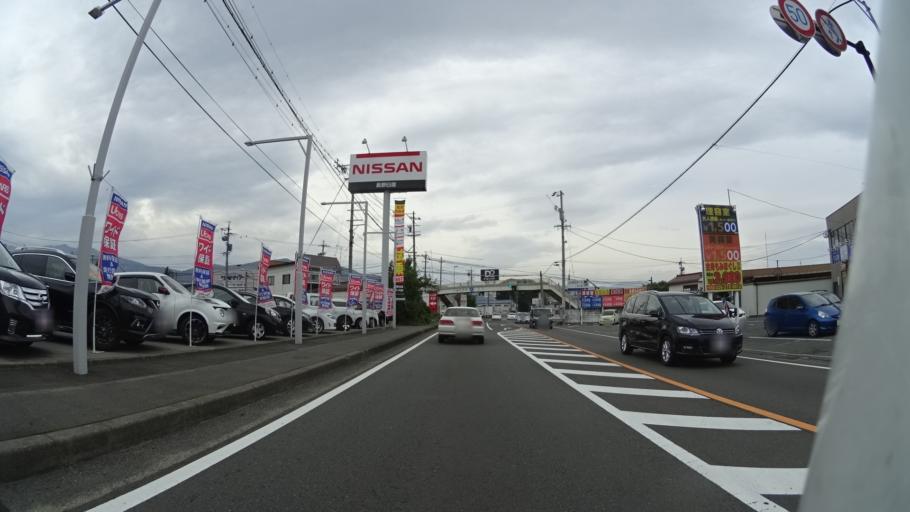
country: JP
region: Nagano
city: Nagano-shi
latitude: 36.5241
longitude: 138.1252
